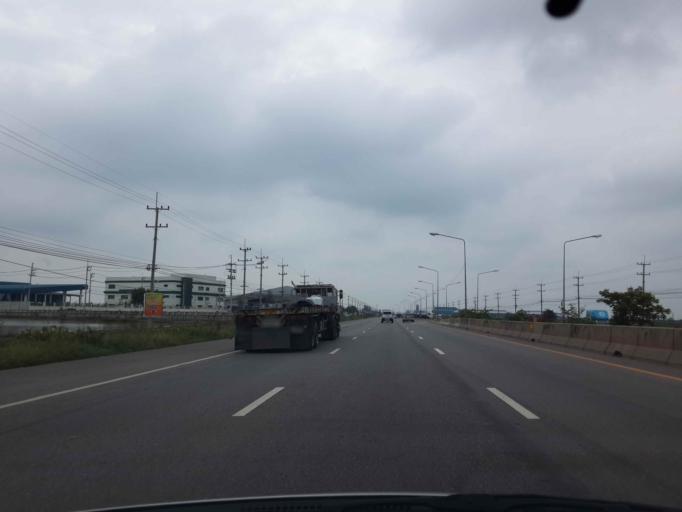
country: TH
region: Samut Songkhram
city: Samut Songkhram
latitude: 13.4629
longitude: 100.0997
